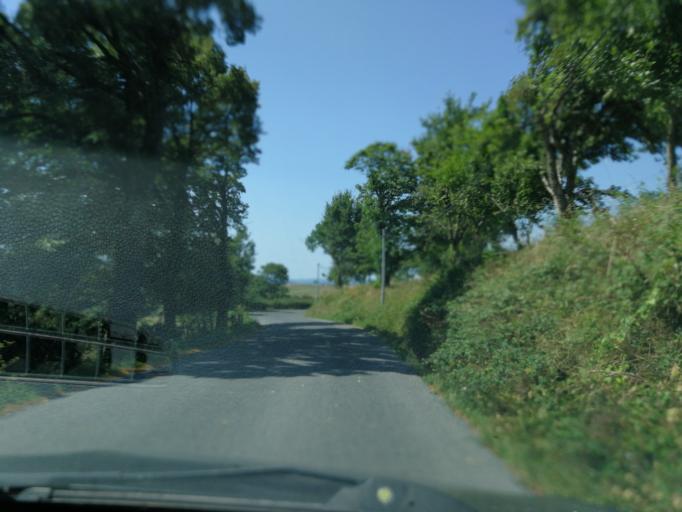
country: FR
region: Midi-Pyrenees
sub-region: Departement de l'Aveyron
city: Livinhac-le-Haut
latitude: 44.6663
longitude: 2.2846
